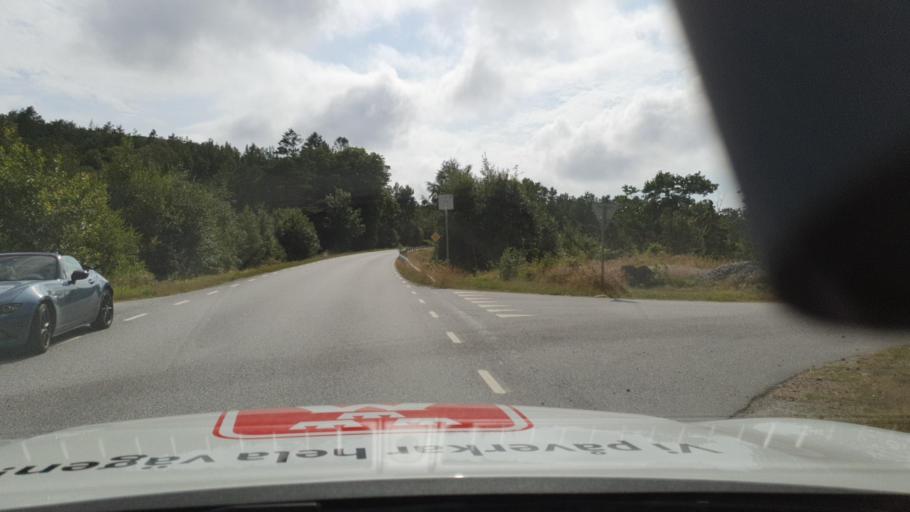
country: SE
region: Vaestra Goetaland
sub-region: Sotenas Kommun
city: Hunnebostrand
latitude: 58.5662
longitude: 11.2977
